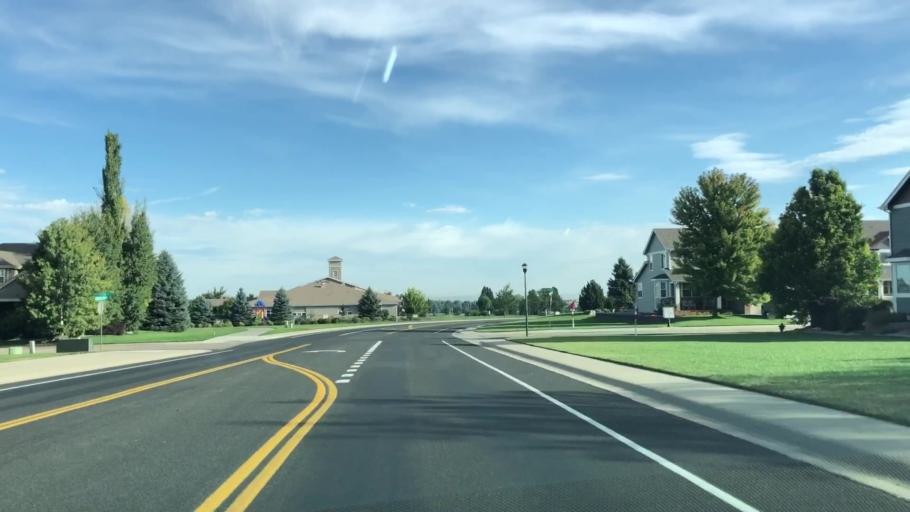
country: US
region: Colorado
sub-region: Weld County
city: Windsor
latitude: 40.4720
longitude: -104.9794
